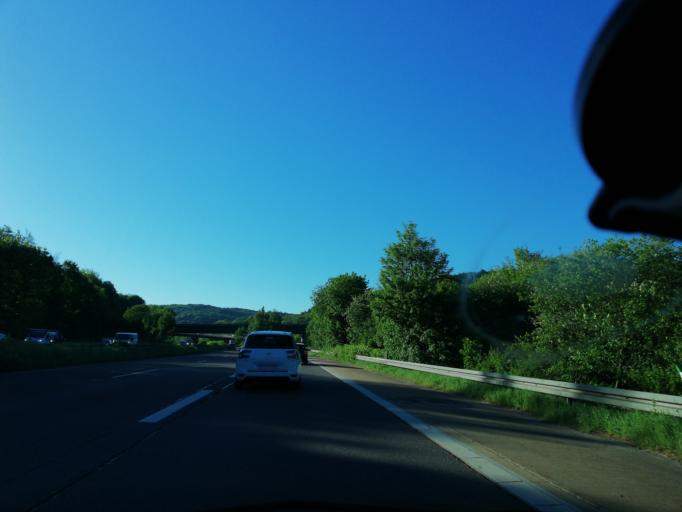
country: DE
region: North Rhine-Westphalia
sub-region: Regierungsbezirk Dusseldorf
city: Solingen
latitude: 51.2325
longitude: 7.0954
